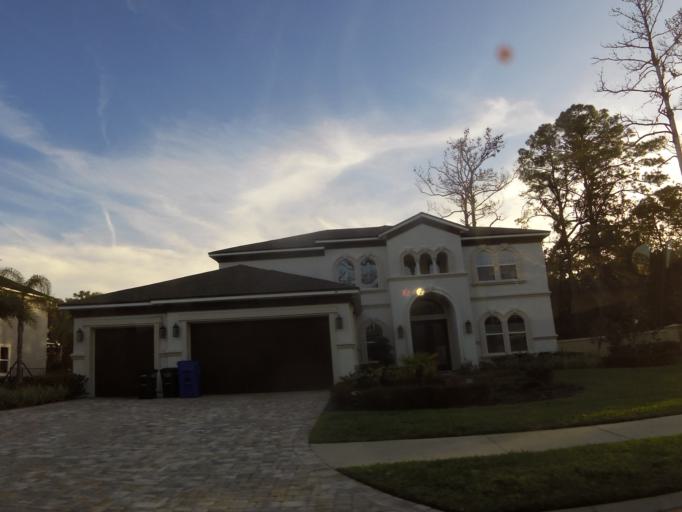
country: US
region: Florida
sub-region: Saint Johns County
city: Palm Valley
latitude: 30.1715
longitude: -81.3860
